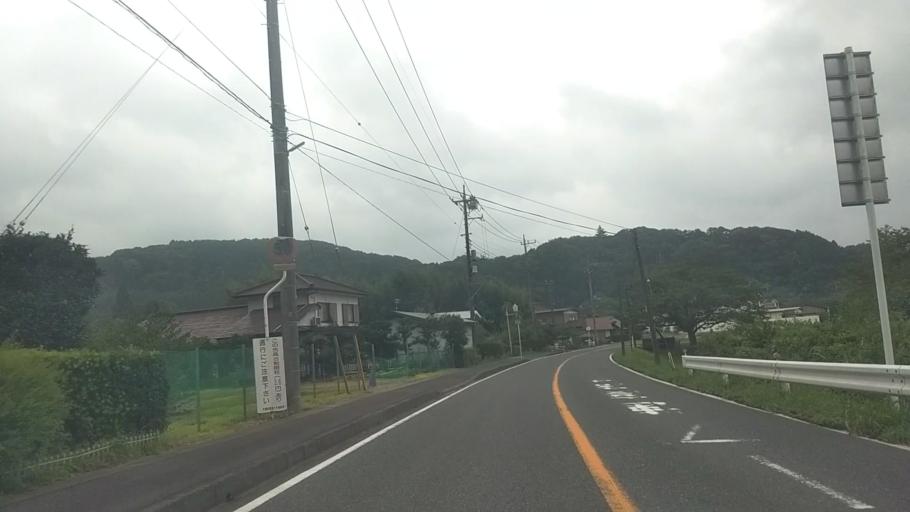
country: JP
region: Chiba
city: Kawaguchi
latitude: 35.2607
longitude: 140.0634
